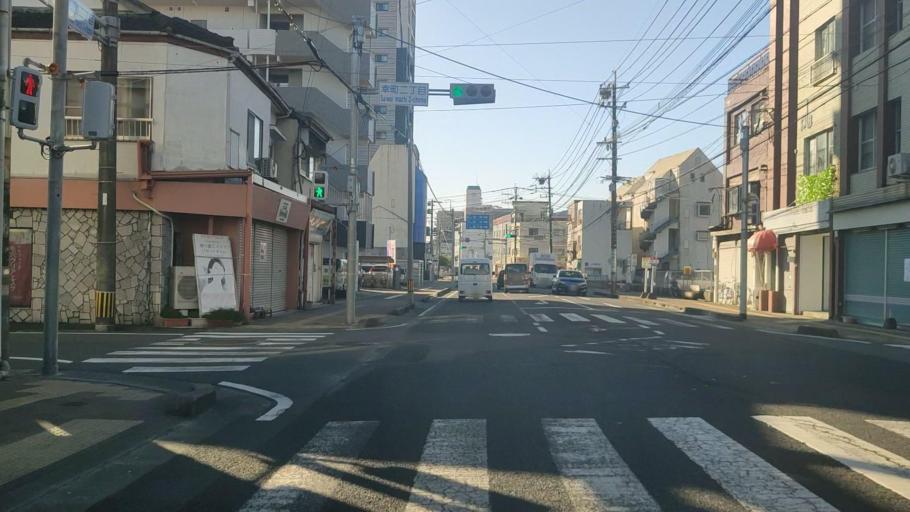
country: JP
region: Miyazaki
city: Nobeoka
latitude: 32.5880
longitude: 131.6711
